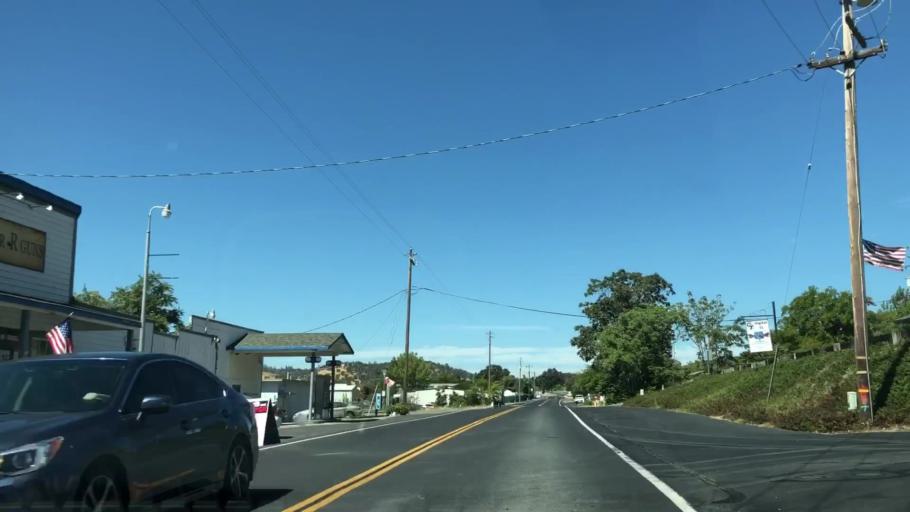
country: US
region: California
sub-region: Calaveras County
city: Copperopolis
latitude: 37.9781
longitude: -120.6383
